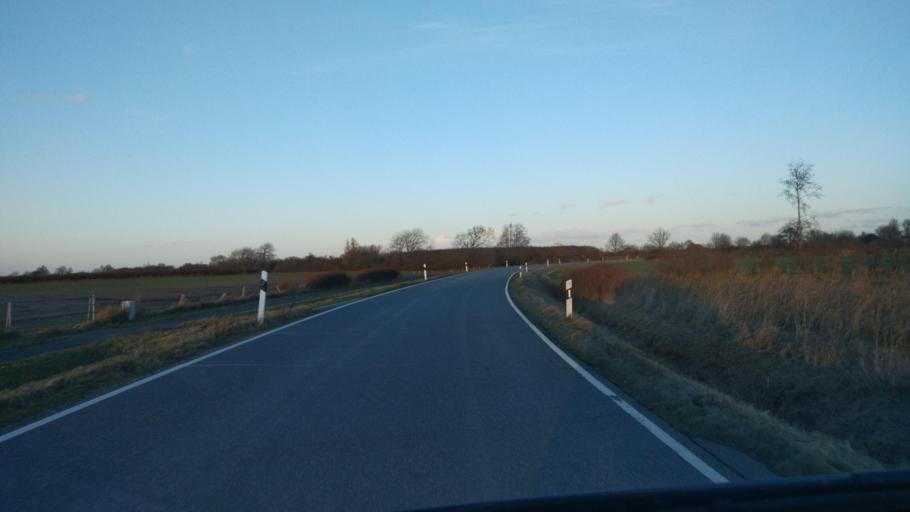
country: DE
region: Schleswig-Holstein
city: Hollingstedt
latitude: 54.4612
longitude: 9.3530
